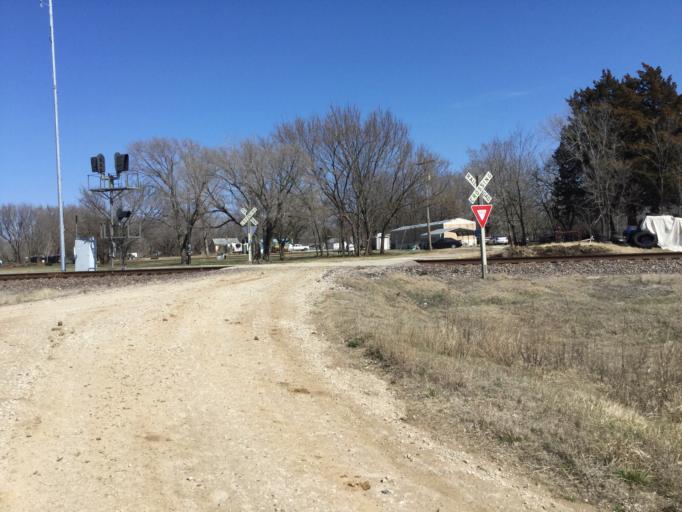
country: US
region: Kansas
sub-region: Wilson County
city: Fredonia
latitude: 37.6268
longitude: -95.7484
